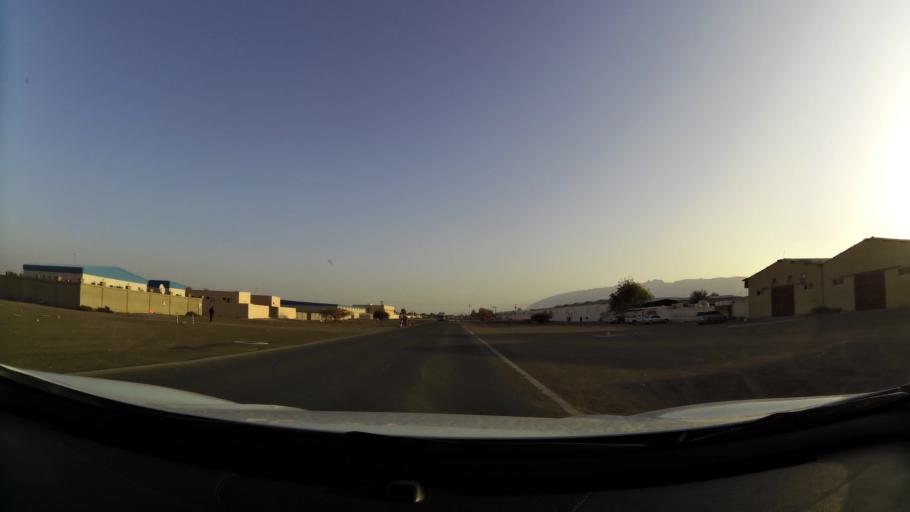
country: AE
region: Abu Dhabi
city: Al Ain
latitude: 24.1521
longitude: 55.8192
